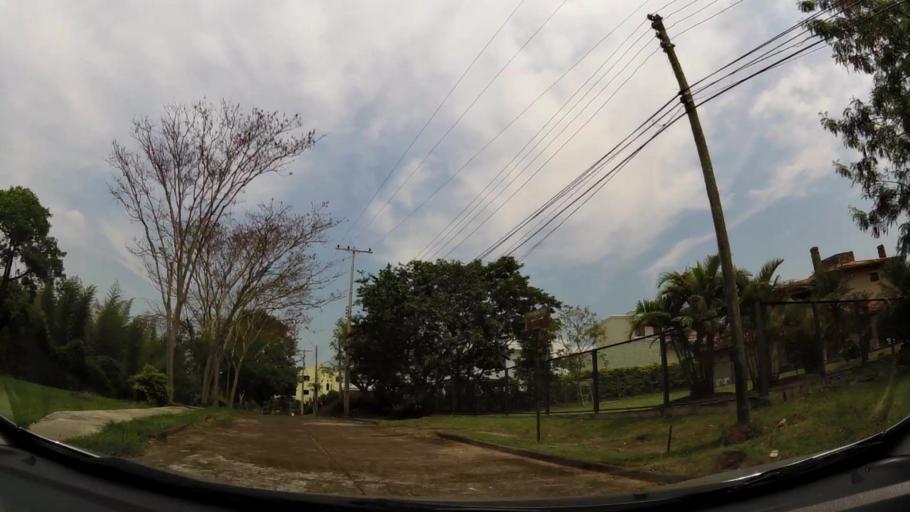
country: PY
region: Alto Parana
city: Ciudad del Este
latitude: -25.4880
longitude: -54.6087
